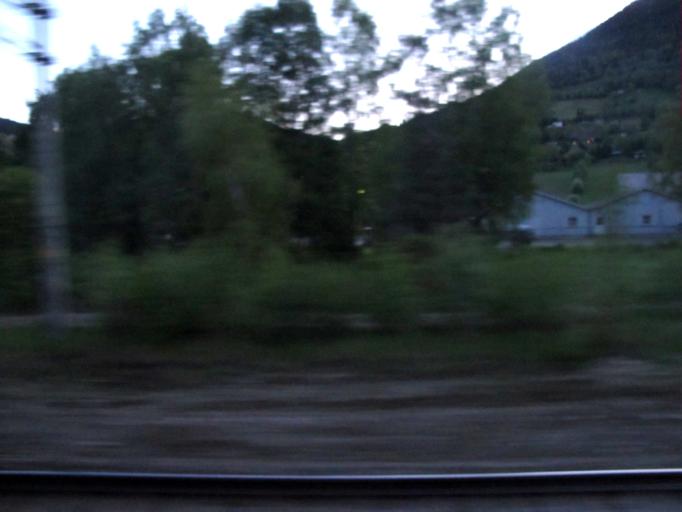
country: NO
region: Oppland
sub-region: Nord-Fron
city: Vinstra
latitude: 61.6644
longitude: 9.6996
